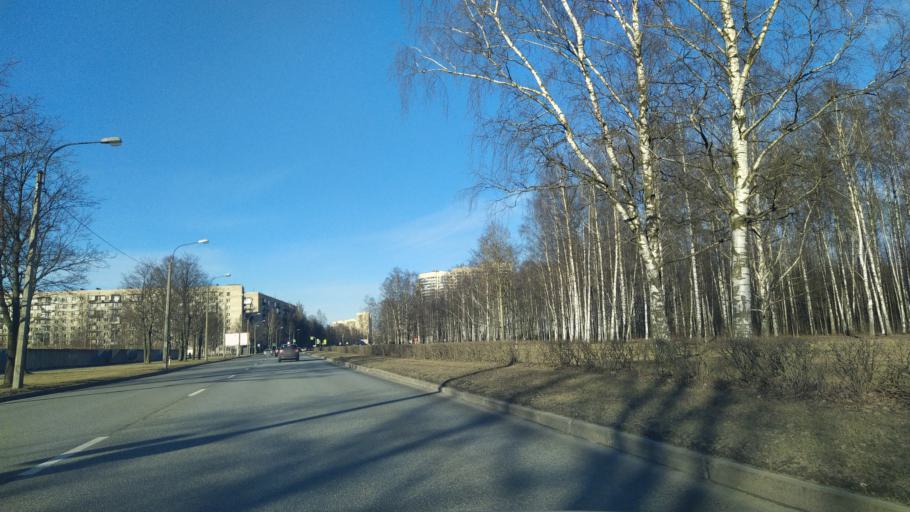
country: RU
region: Leningrad
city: Kalininskiy
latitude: 59.9978
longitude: 30.3933
